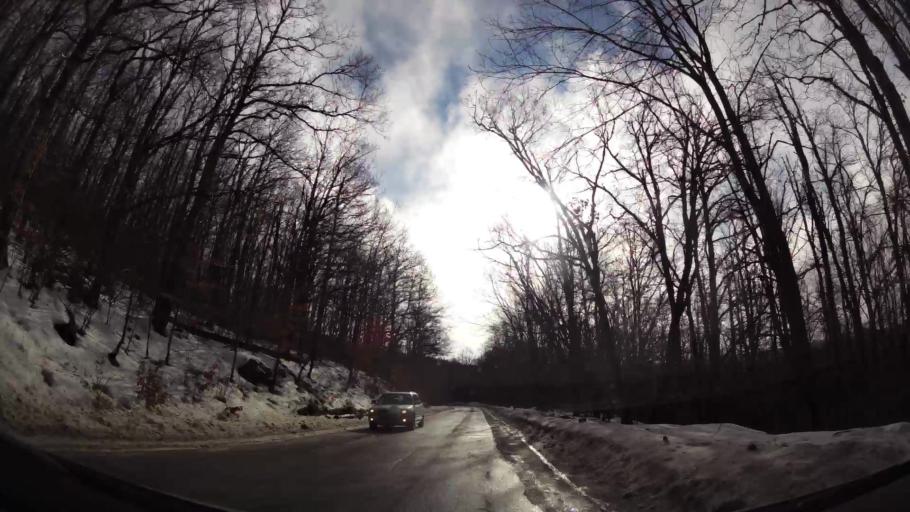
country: BG
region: Sofia-Capital
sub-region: Stolichna Obshtina
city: Sofia
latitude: 42.6331
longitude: 23.2283
